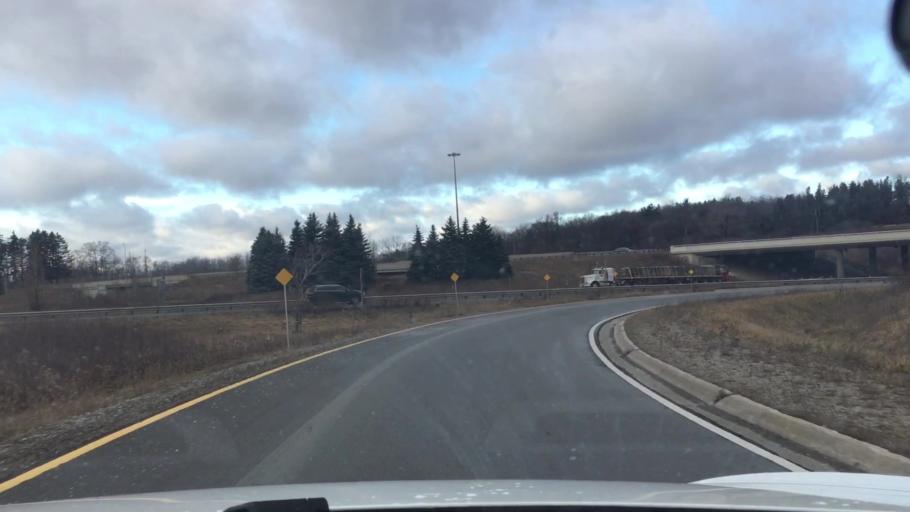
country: CA
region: Ontario
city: Ancaster
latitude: 43.2309
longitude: -79.9509
